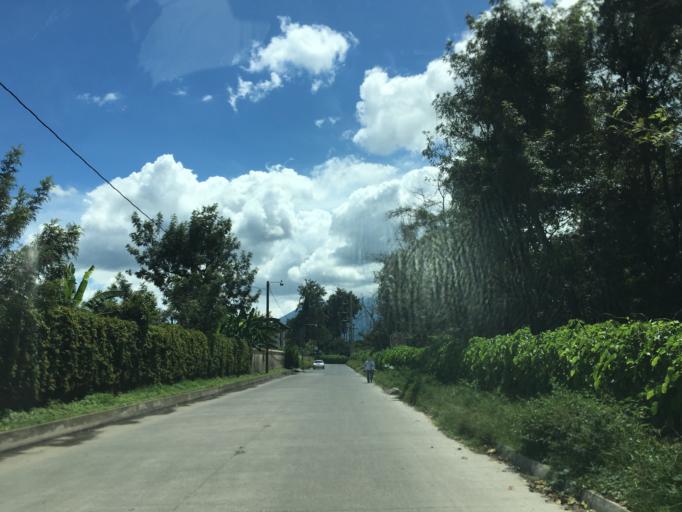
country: GT
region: Sacatepequez
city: Antigua Guatemala
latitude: 14.5439
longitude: -90.7341
